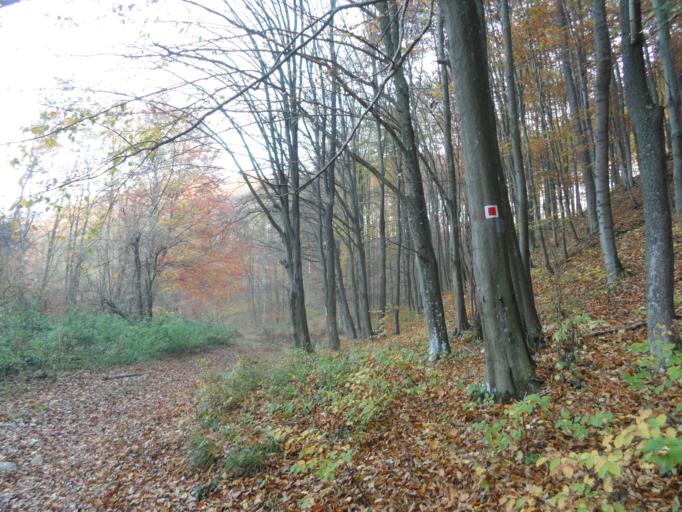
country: HU
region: Veszprem
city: Herend
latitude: 47.2282
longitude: 17.7404
